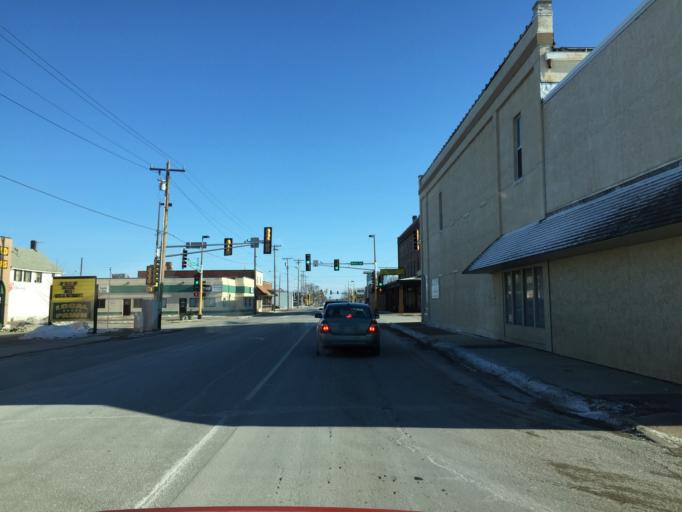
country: US
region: Minnesota
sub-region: Isanti County
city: Cambridge
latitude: 45.5727
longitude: -93.2249
